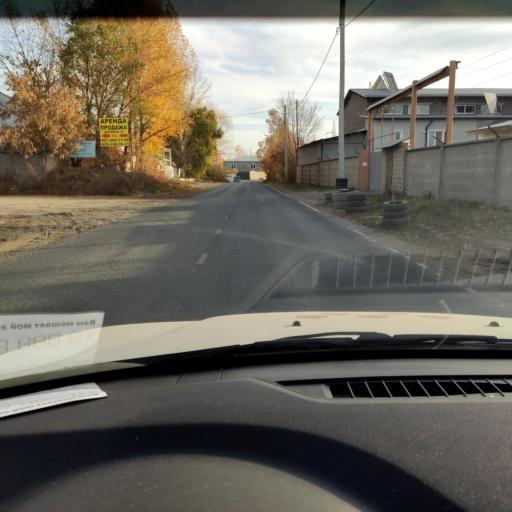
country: RU
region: Samara
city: Zhigulevsk
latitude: 53.5162
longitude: 49.4750
